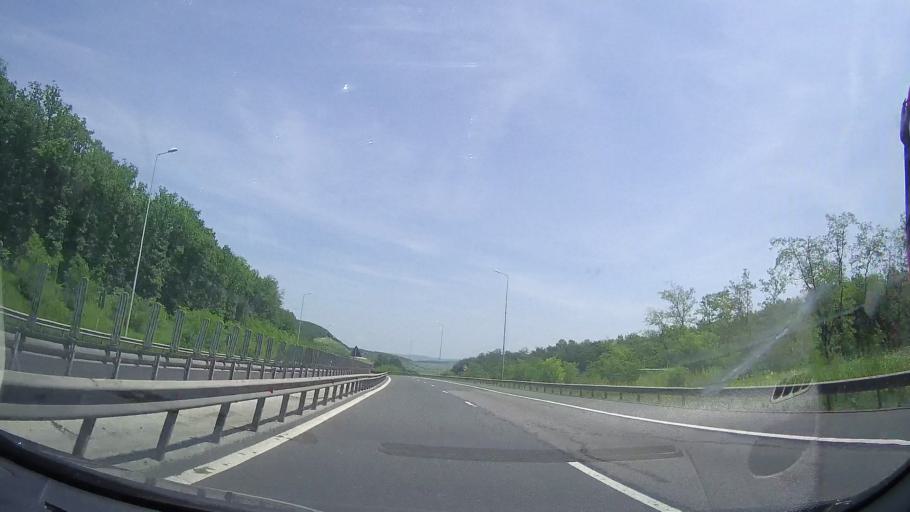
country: RO
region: Sibiu
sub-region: Comuna Orlat
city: Orlat
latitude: 45.7794
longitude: 23.9647
